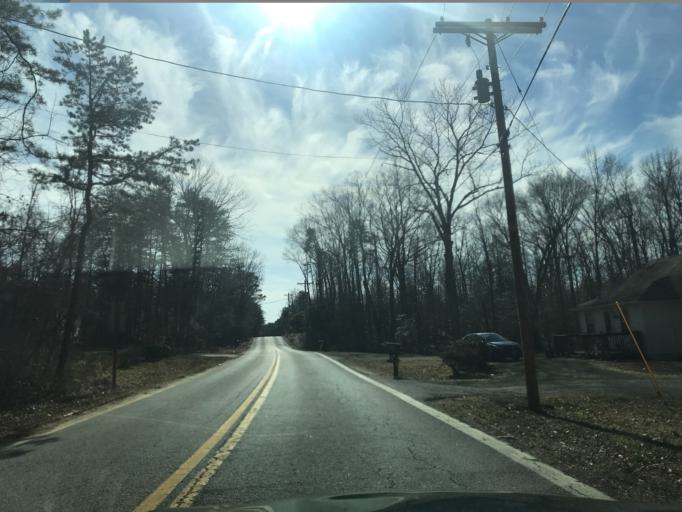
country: US
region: Maryland
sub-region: Charles County
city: Indian Head
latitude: 38.4907
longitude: -77.1607
